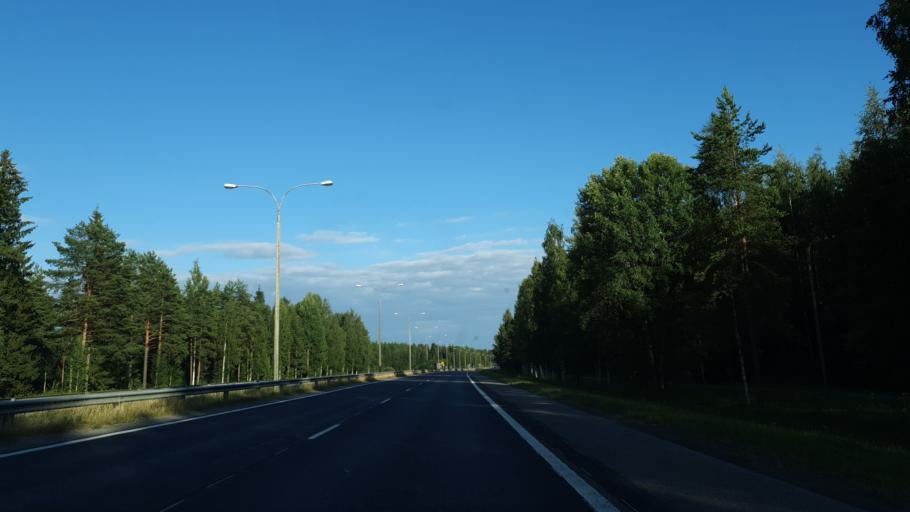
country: FI
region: North Karelia
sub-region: Joensuu
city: Joensuu
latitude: 62.6245
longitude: 29.7122
